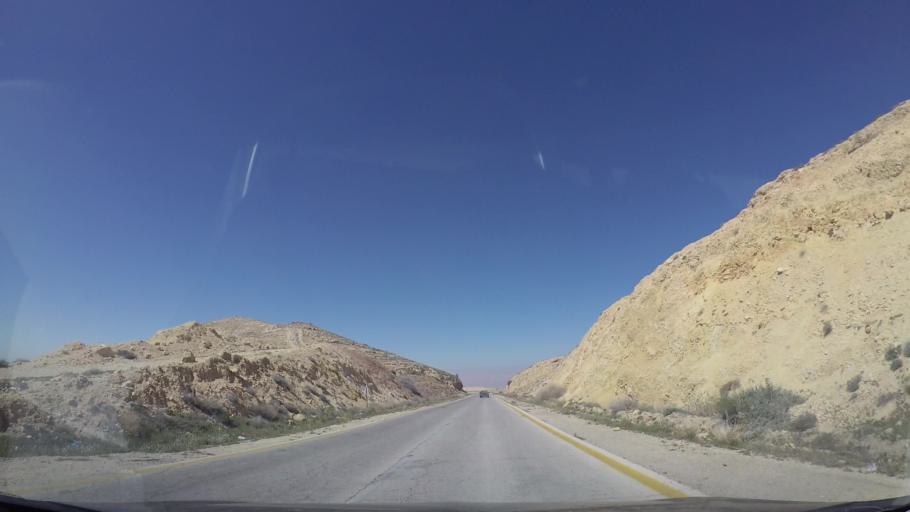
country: JO
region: Tafielah
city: At Tafilah
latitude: 30.8572
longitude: 35.5449
